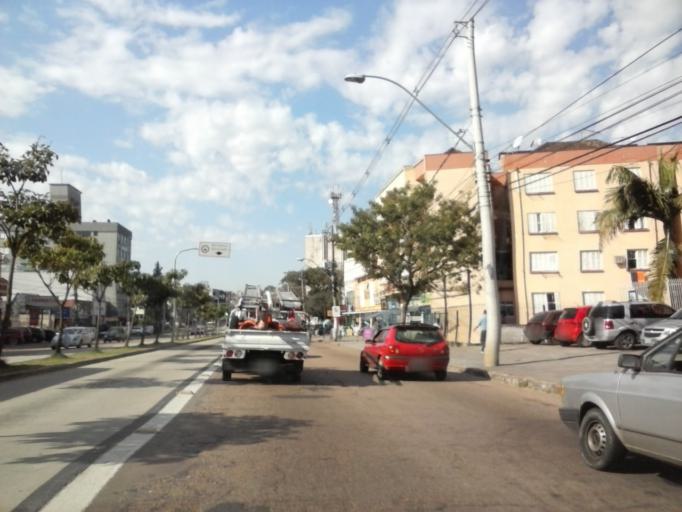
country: BR
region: Rio Grande do Sul
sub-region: Porto Alegre
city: Porto Alegre
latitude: -30.0404
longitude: -51.1656
